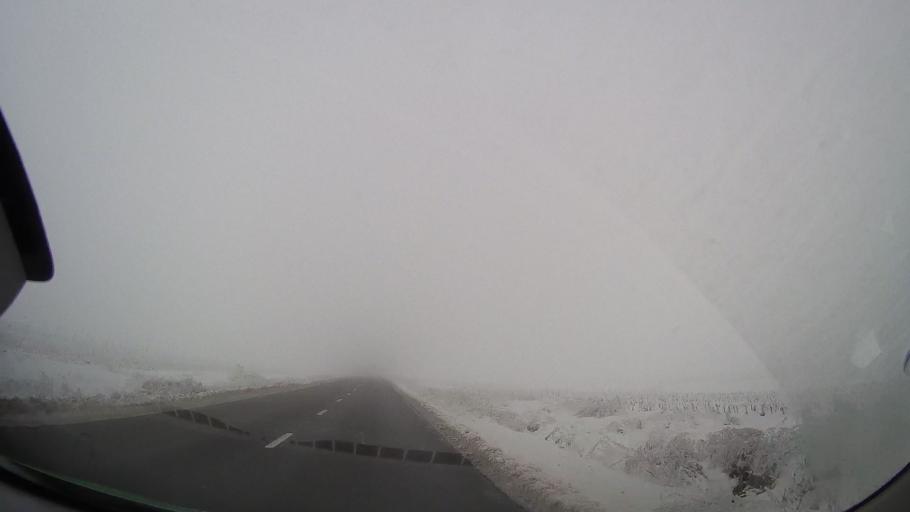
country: RO
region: Neamt
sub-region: Comuna Sabaoani
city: Sabaoani
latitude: 47.0363
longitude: 26.8542
